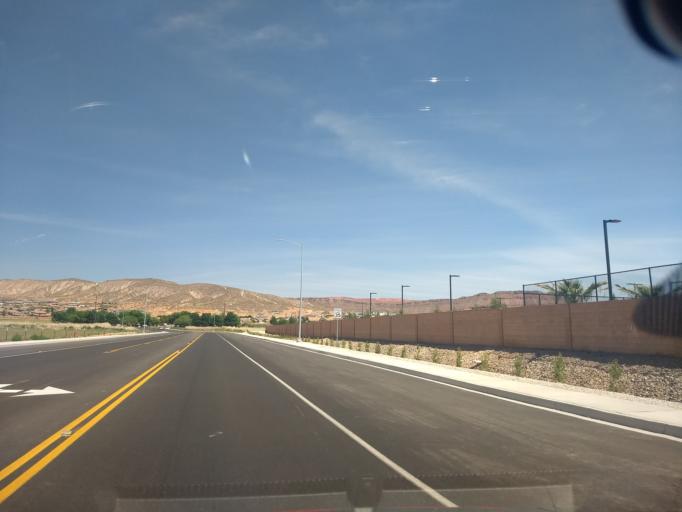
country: US
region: Utah
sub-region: Washington County
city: Washington
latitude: 37.0943
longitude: -113.5040
